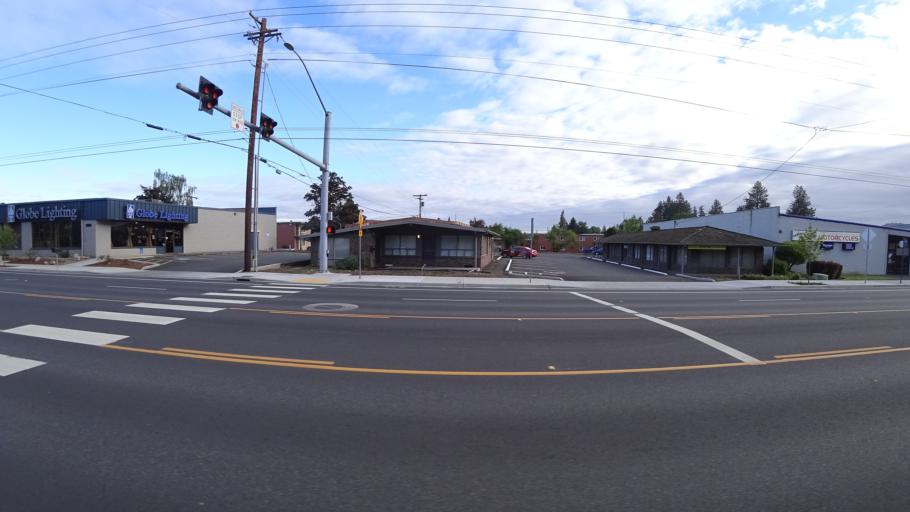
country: US
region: Oregon
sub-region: Washington County
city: Beaverton
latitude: 45.4868
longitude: -122.8187
